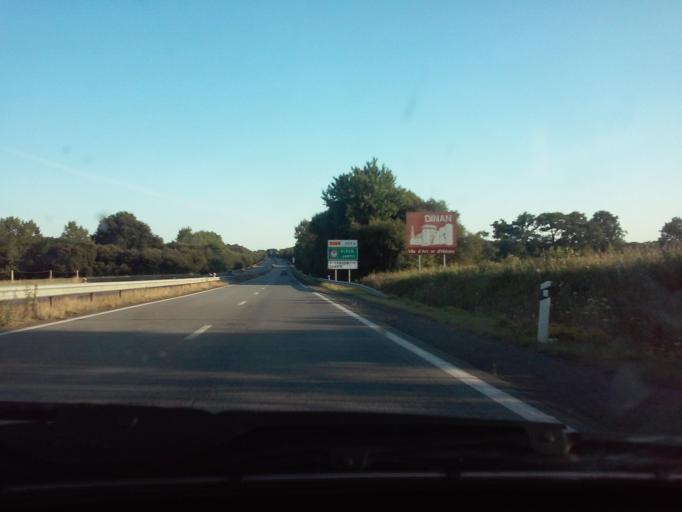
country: FR
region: Brittany
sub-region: Departement des Cotes-d'Armor
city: Saint-Samson-sur-Rance
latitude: 48.5003
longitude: -2.0400
